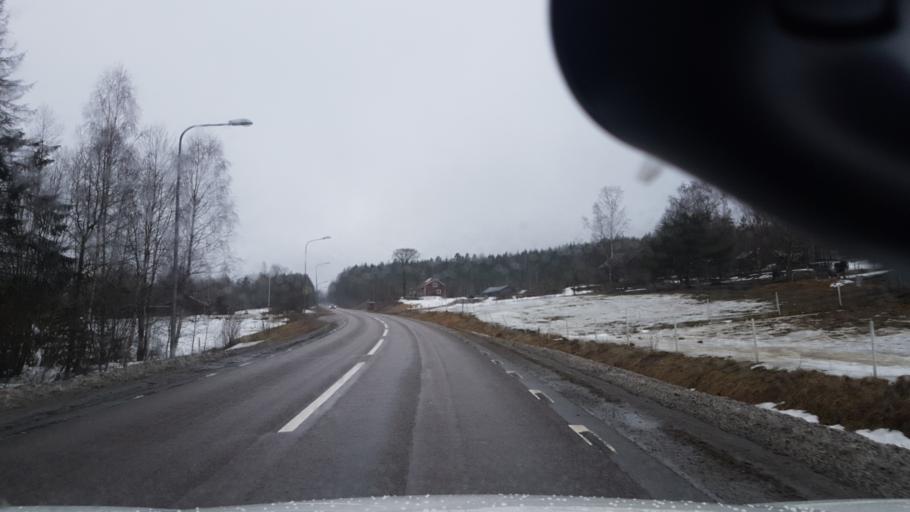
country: SE
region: Vaermland
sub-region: Arvika Kommun
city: Arvika
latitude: 59.6466
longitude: 12.7754
